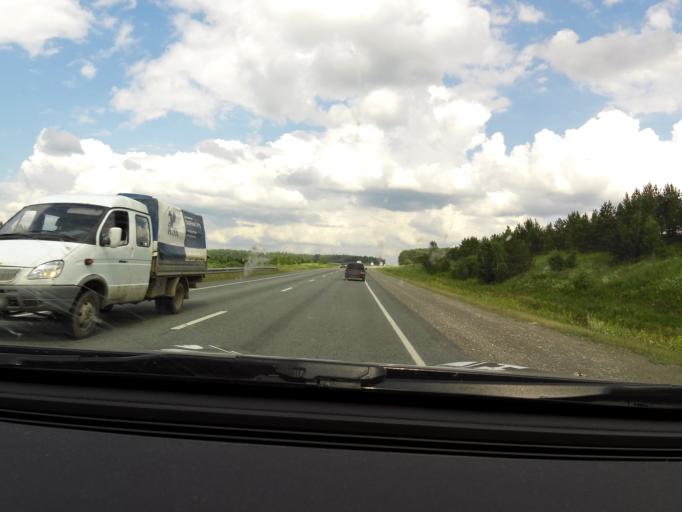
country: RU
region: Sverdlovsk
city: Bisert'
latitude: 56.8064
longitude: 58.7200
